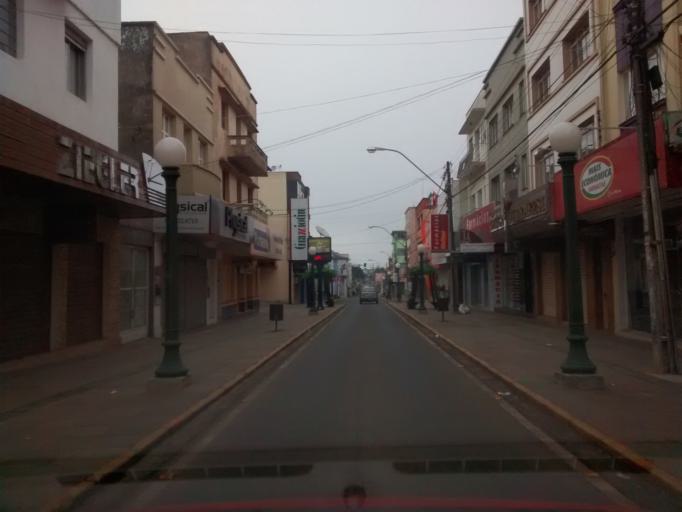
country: BR
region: Rio Grande do Sul
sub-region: Vacaria
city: Vacaria
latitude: -28.5041
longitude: -50.9381
